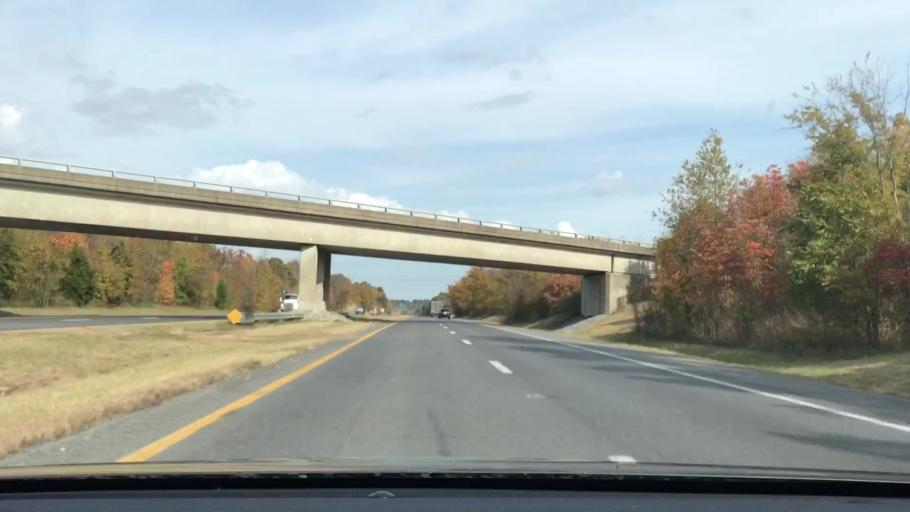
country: US
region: Kentucky
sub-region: Marshall County
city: Calvert City
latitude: 36.9676
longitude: -88.3473
